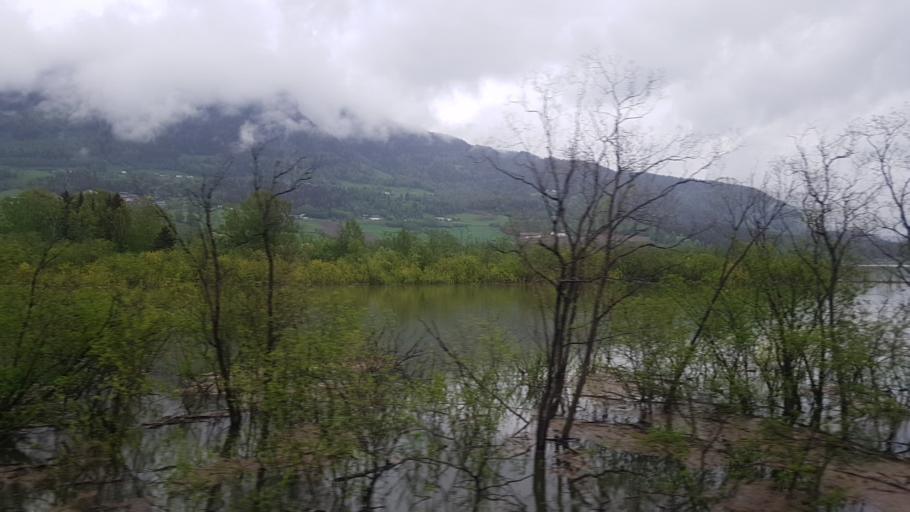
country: NO
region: Oppland
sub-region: Ringebu
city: Ringebu
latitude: 61.4536
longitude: 10.2048
